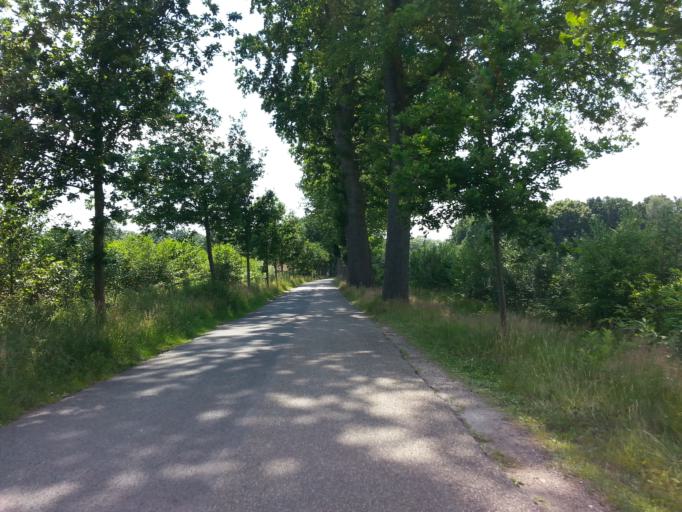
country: NL
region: Utrecht
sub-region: Gemeente Amersfoort
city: Randenbroek
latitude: 52.1166
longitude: 5.3947
